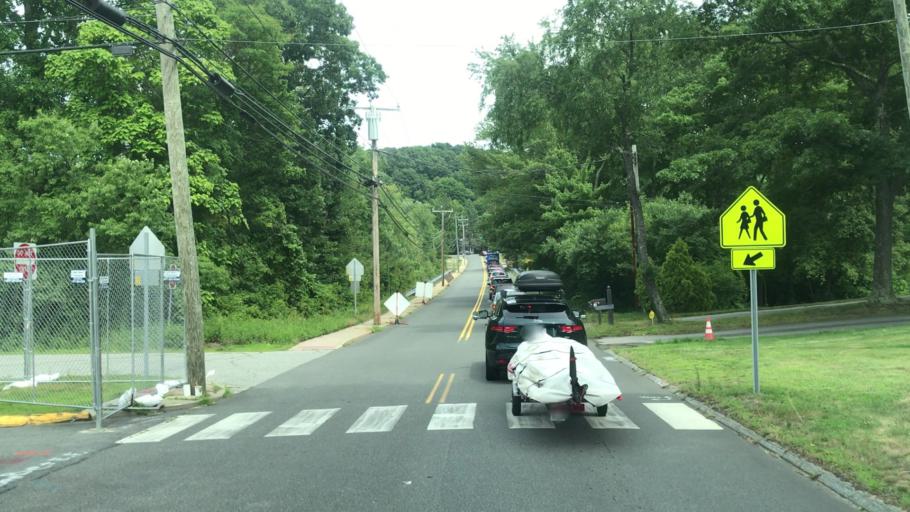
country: US
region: Connecticut
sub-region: New London County
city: Niantic
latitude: 41.3469
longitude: -72.2131
